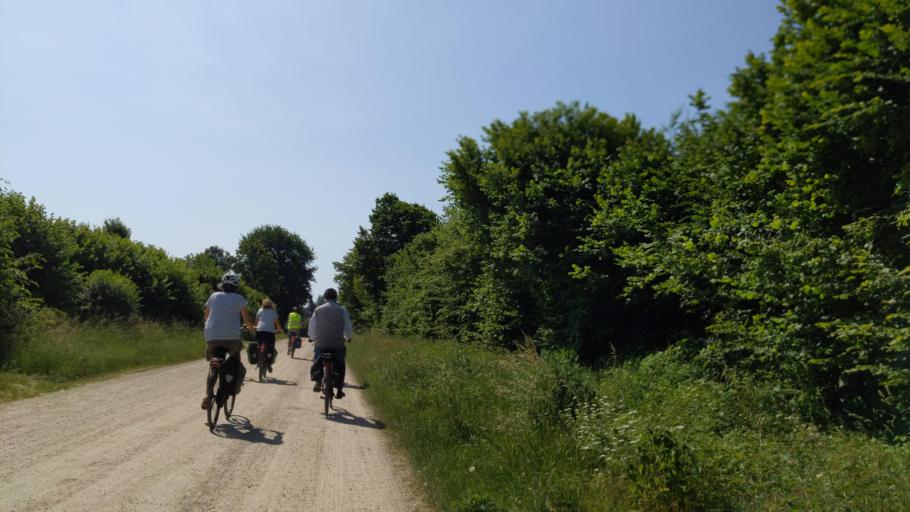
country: DE
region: Schleswig-Holstein
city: Klempau
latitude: 53.7638
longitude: 10.6540
